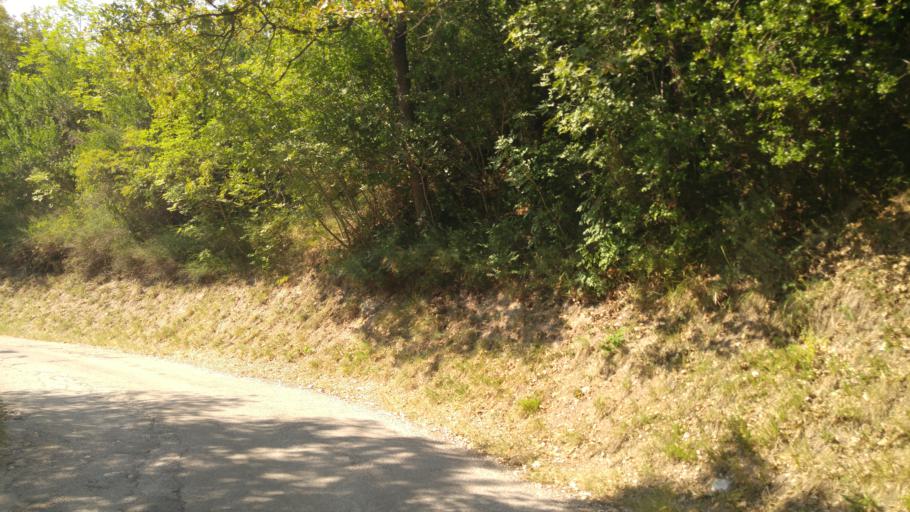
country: IT
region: The Marches
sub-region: Provincia di Pesaro e Urbino
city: Fossombrone
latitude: 43.6793
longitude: 12.8049
